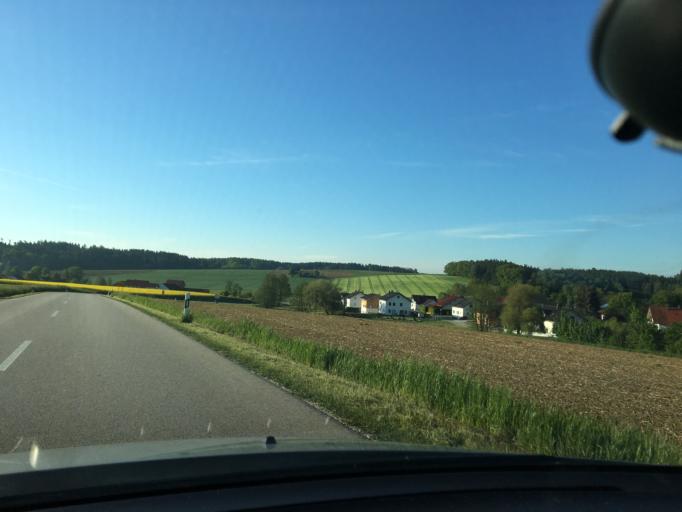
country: DE
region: Bavaria
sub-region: Lower Bavaria
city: Vilsbiburg
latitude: 48.5022
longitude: 12.3468
